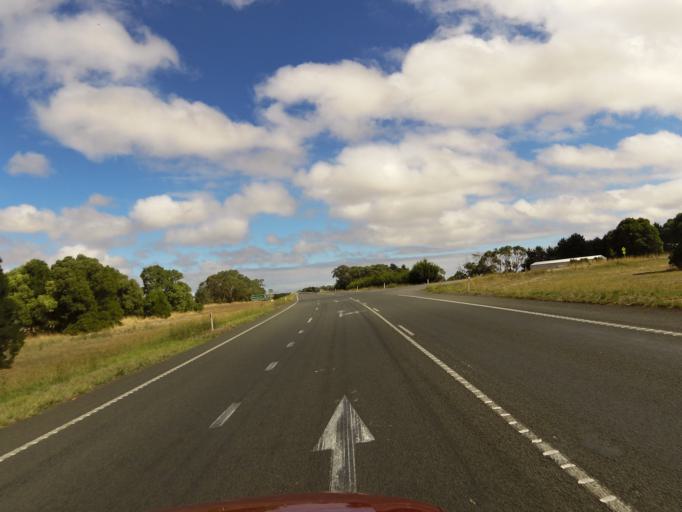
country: AU
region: Victoria
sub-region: Warrnambool
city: Allansford
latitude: -38.3390
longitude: 142.7025
